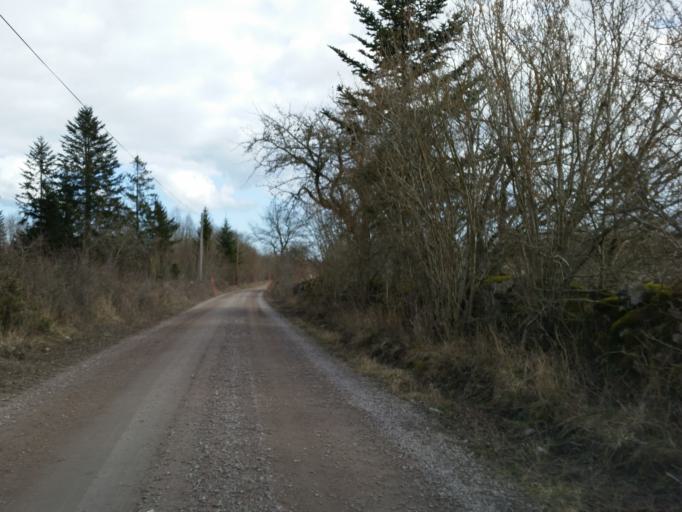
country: SE
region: Kalmar
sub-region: Morbylanga Kommun
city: Sodra Sandby
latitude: 56.6780
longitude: 16.6011
